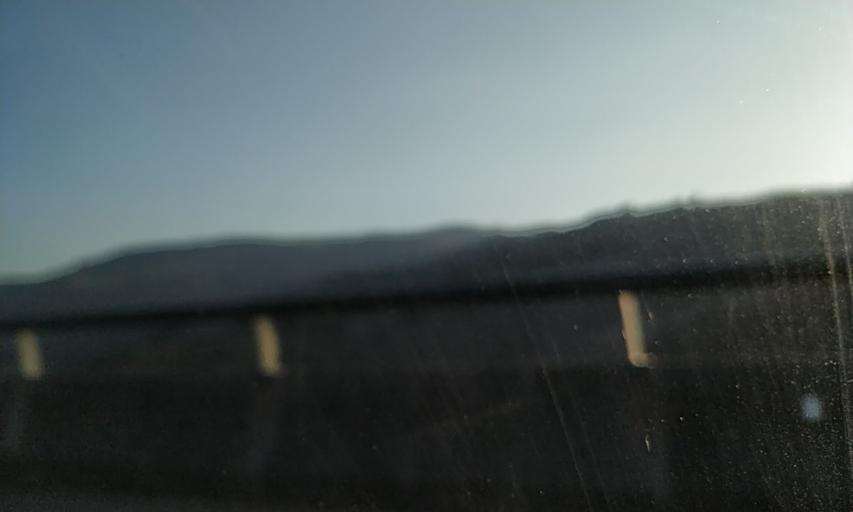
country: ES
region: Galicia
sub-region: Provincia de Lugo
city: Becerrea
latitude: 42.8411
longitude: -7.1184
